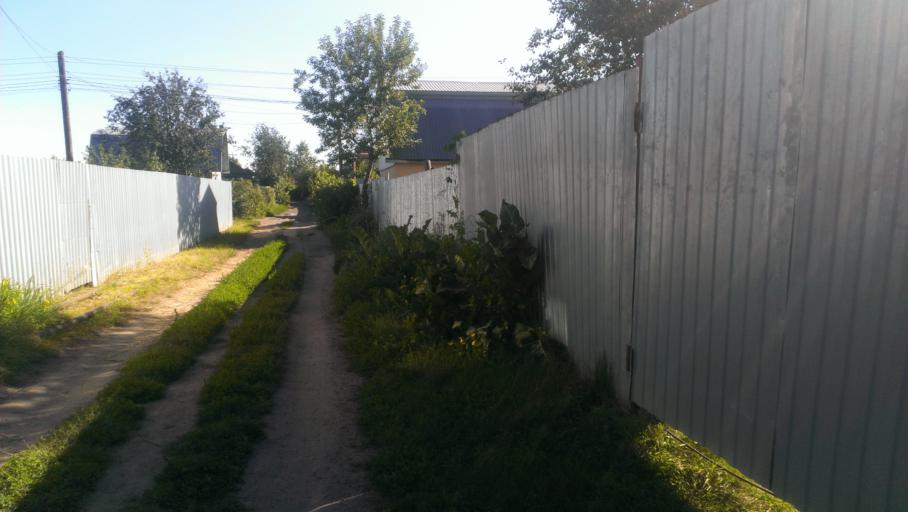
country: RU
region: Altai Krai
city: Novosilikatnyy
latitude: 53.3241
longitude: 83.6696
